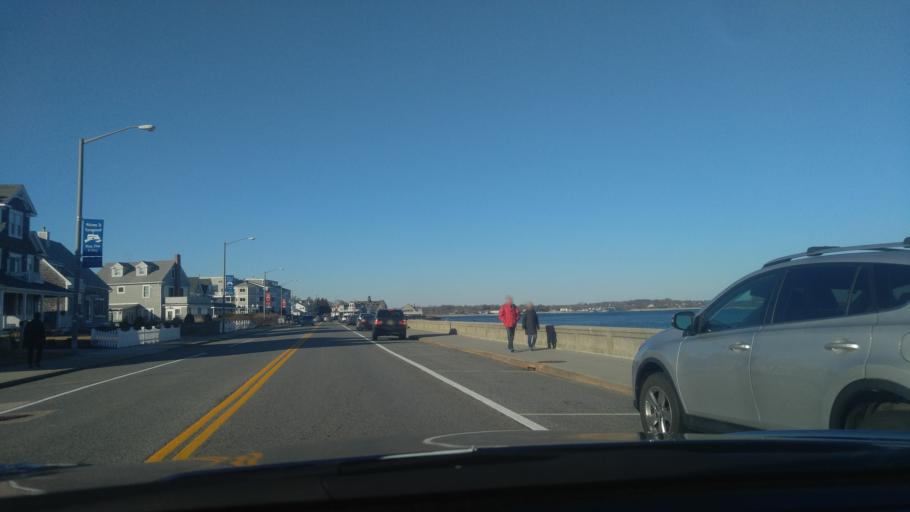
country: US
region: Rhode Island
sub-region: Washington County
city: Narragansett Pier
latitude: 41.4250
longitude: -71.4558
